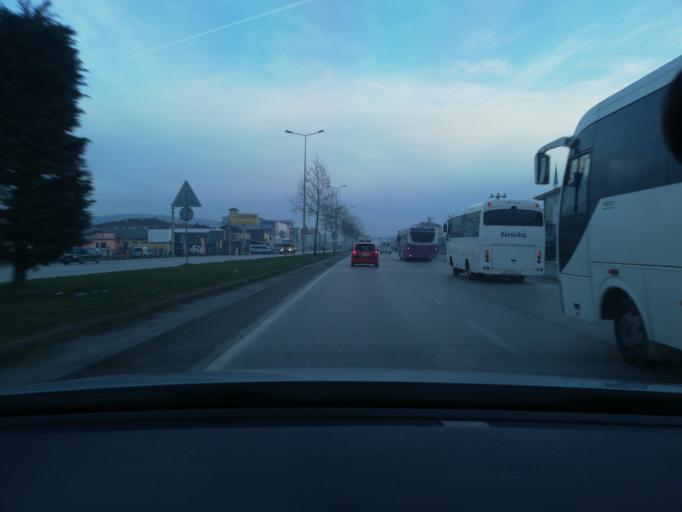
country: TR
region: Duzce
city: Duzce
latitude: 40.8563
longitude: 31.1667
